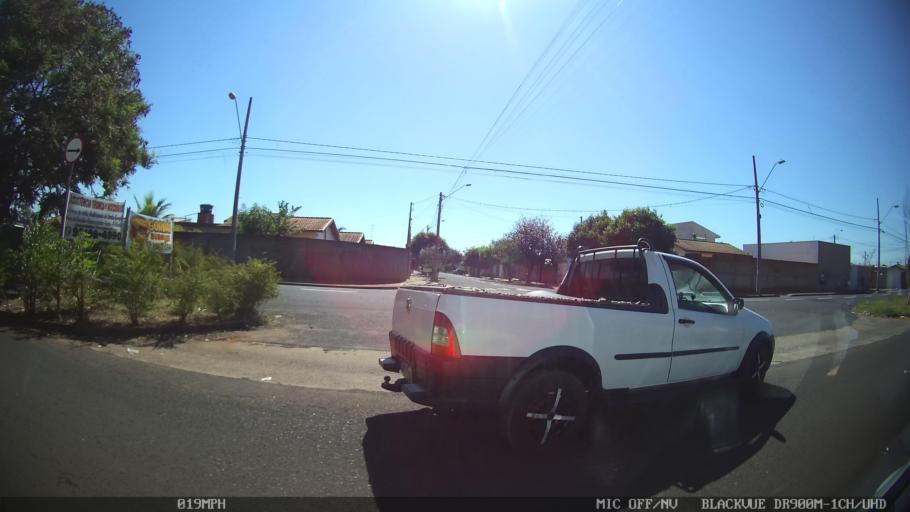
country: BR
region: Sao Paulo
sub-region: Sao Jose Do Rio Preto
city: Sao Jose do Rio Preto
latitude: -20.7405
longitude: -49.4175
